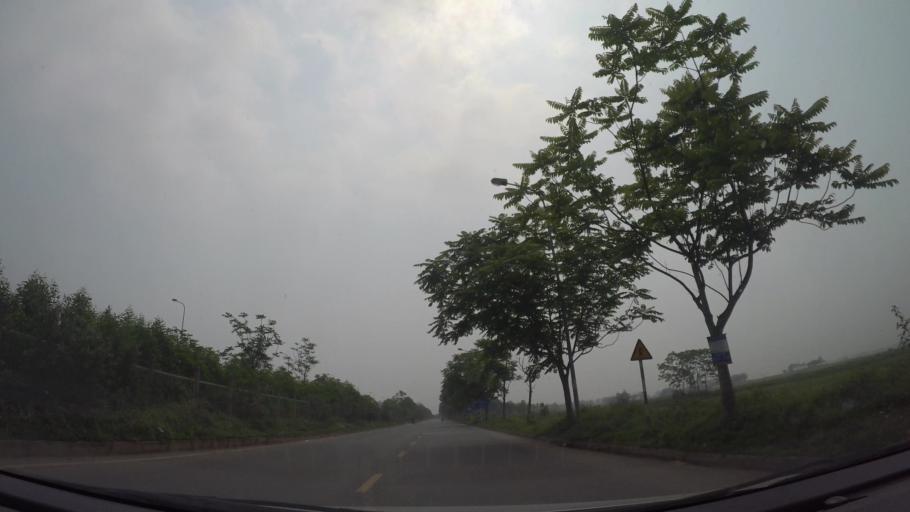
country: VN
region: Ha Noi
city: Lien Quan
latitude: 20.9889
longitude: 105.5657
